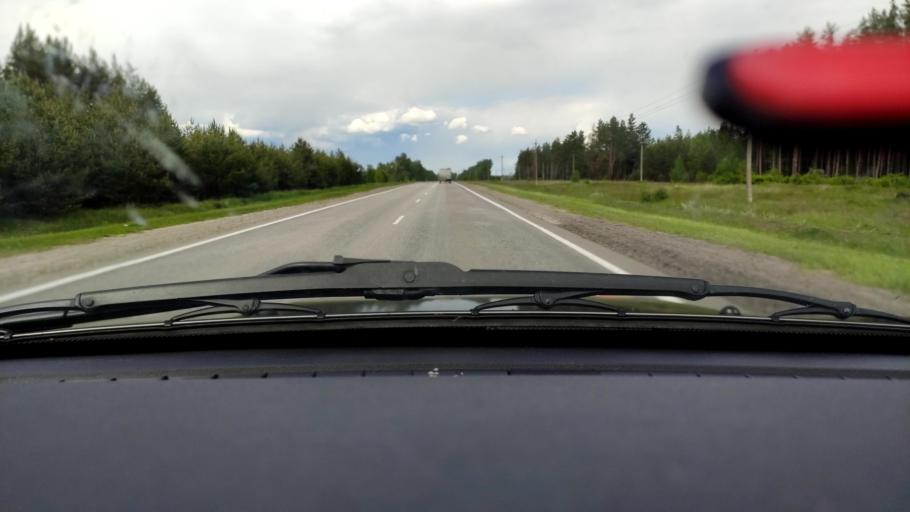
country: RU
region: Voronezj
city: Uryv-Pokrovka
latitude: 51.0564
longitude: 38.9889
